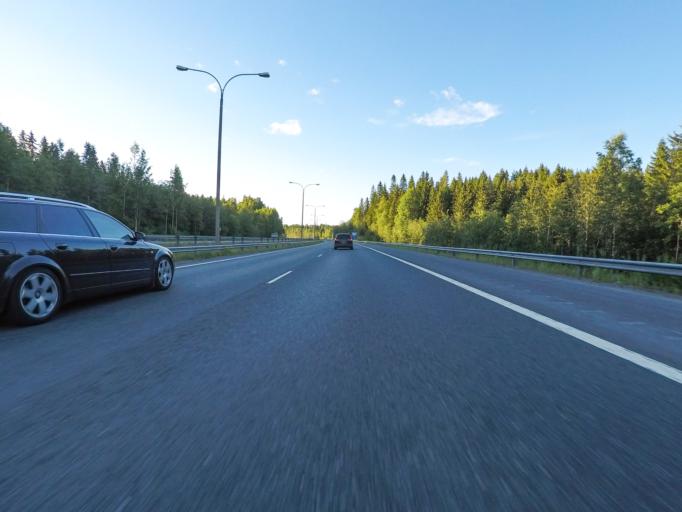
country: FI
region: Northern Savo
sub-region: Kuopio
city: Kuopio
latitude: 62.8493
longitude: 27.6200
